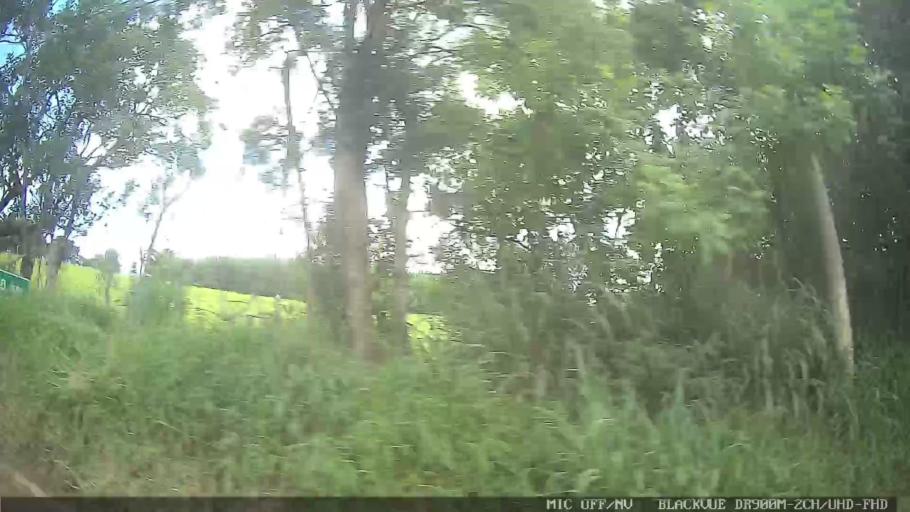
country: BR
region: Sao Paulo
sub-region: Braganca Paulista
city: Braganca Paulista
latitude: -22.9853
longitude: -46.4825
